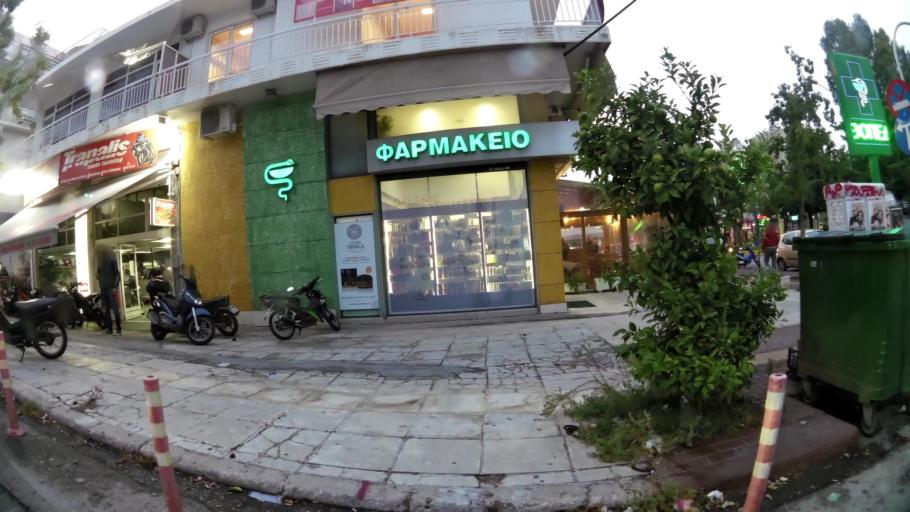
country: GR
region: Attica
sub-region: Nomarchia Athinas
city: Ymittos
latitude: 37.9422
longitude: 23.7489
